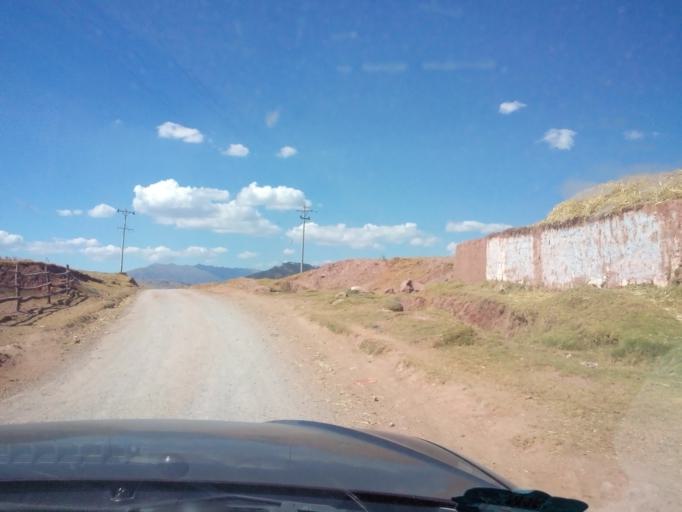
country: PE
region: Cusco
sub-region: Provincia de Anta
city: Huarocondo
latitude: -13.4067
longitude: -72.1648
